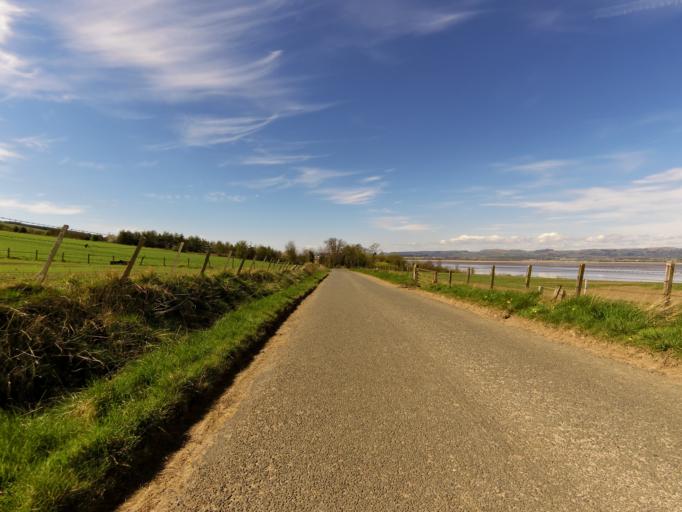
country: GB
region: Scotland
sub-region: Perth and Kinross
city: Errol
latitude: 56.3823
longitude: -3.1254
